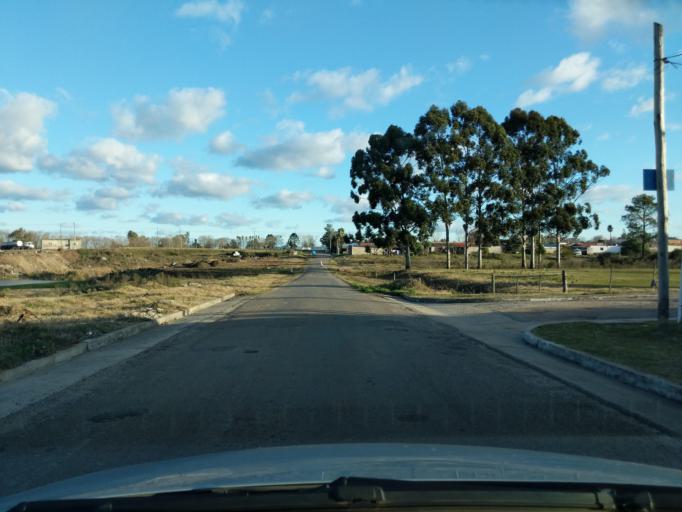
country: UY
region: Florida
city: Florida
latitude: -34.1025
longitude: -56.2276
